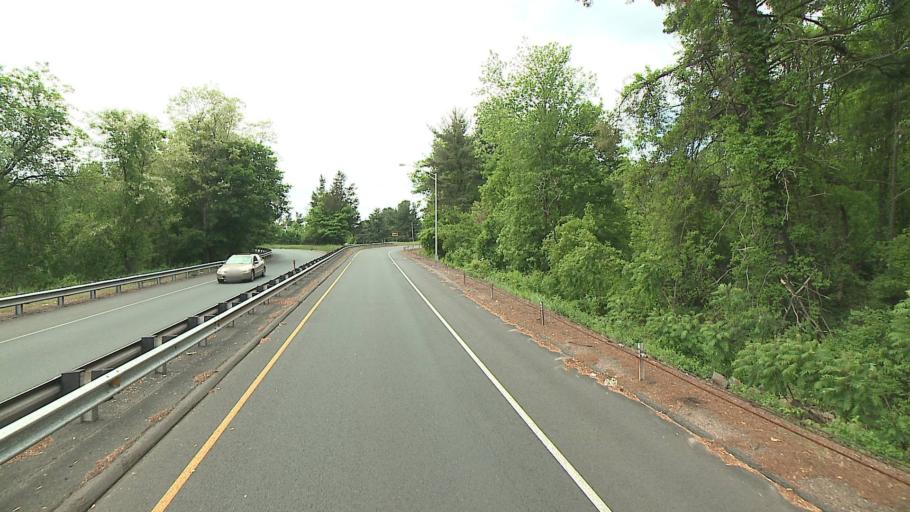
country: US
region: Connecticut
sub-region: Hartford County
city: Thompsonville
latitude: 41.9914
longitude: -72.5891
